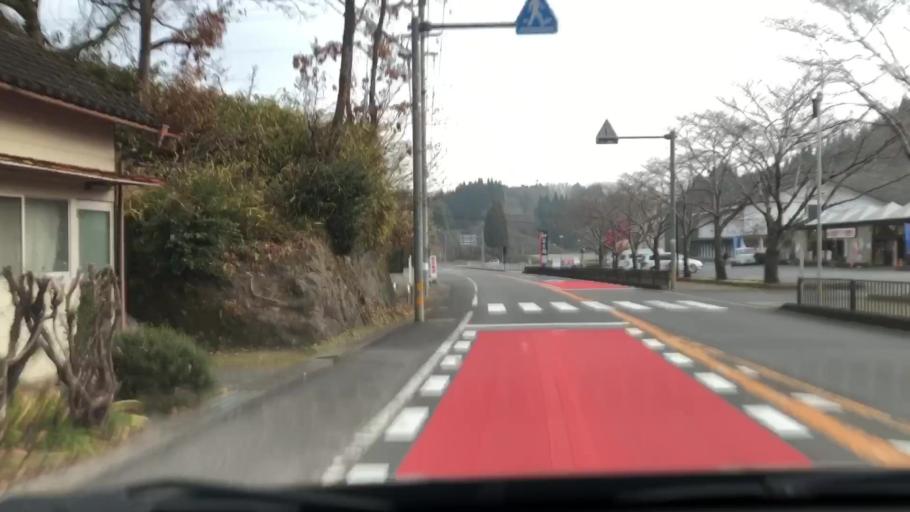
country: JP
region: Oita
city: Takedamachi
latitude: 32.9717
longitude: 131.5175
